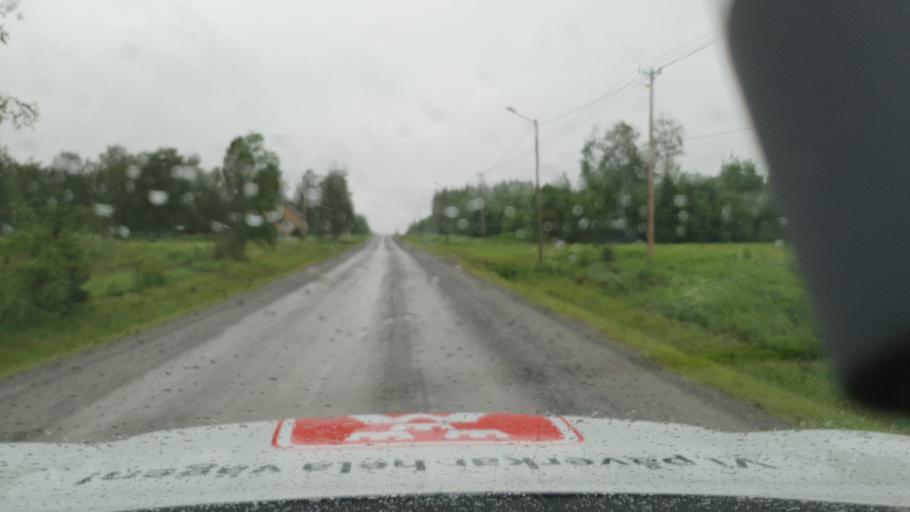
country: SE
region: Vaesterbotten
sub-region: Bjurholms Kommun
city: Bjurholm
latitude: 63.8724
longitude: 19.4544
